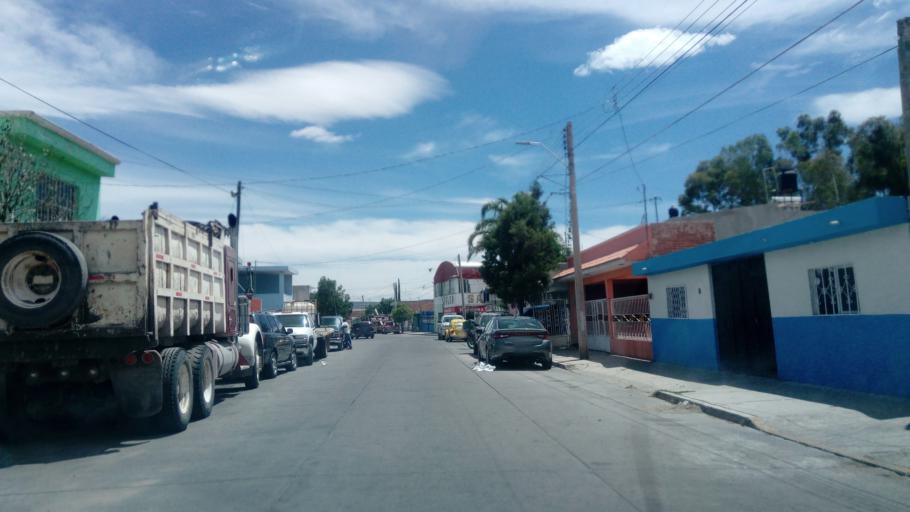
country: MX
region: Durango
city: Victoria de Durango
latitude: 23.9964
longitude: -104.6761
